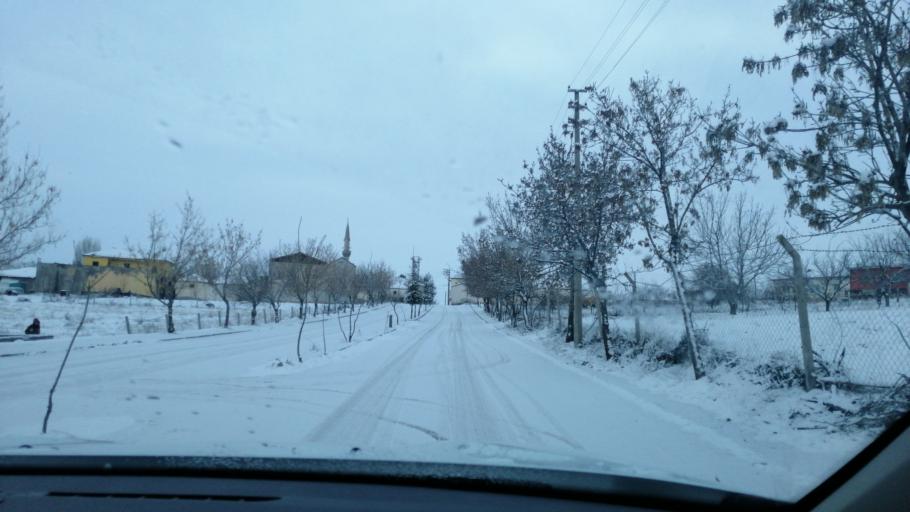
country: TR
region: Aksaray
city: Agacoren
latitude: 38.9287
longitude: 33.9549
